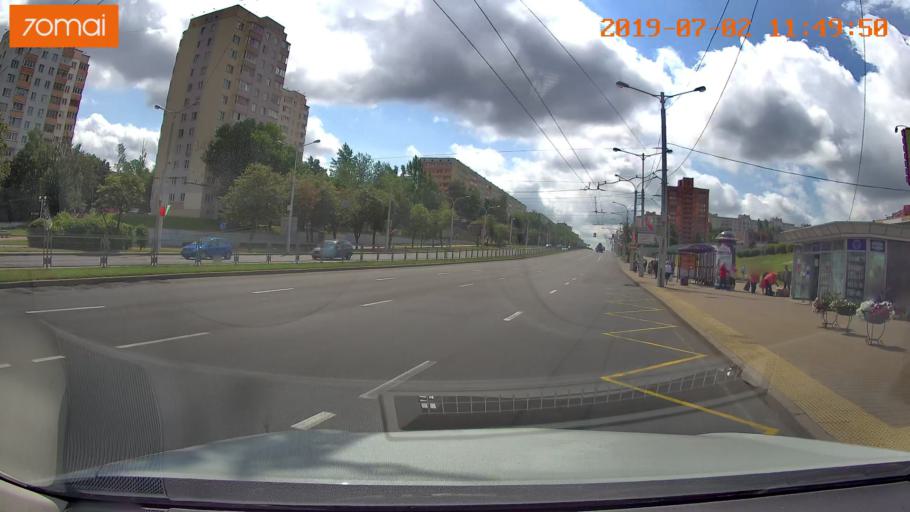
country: BY
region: Minsk
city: Novoye Medvezhino
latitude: 53.9091
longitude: 27.4953
